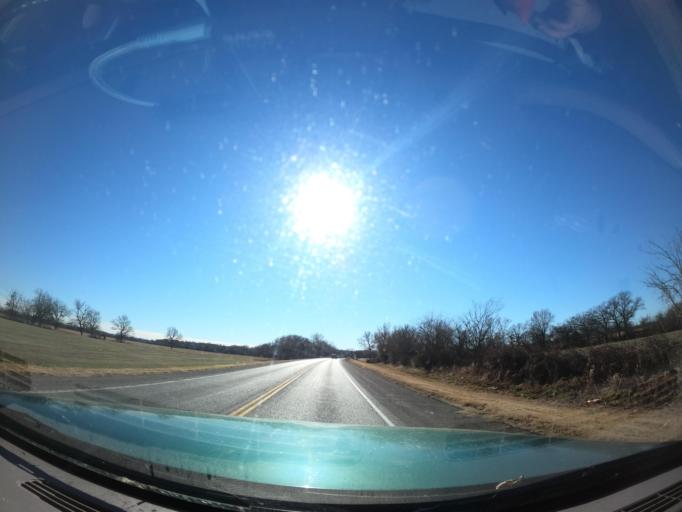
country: US
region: Oklahoma
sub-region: Muskogee County
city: Haskell
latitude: 35.8798
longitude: -95.6608
